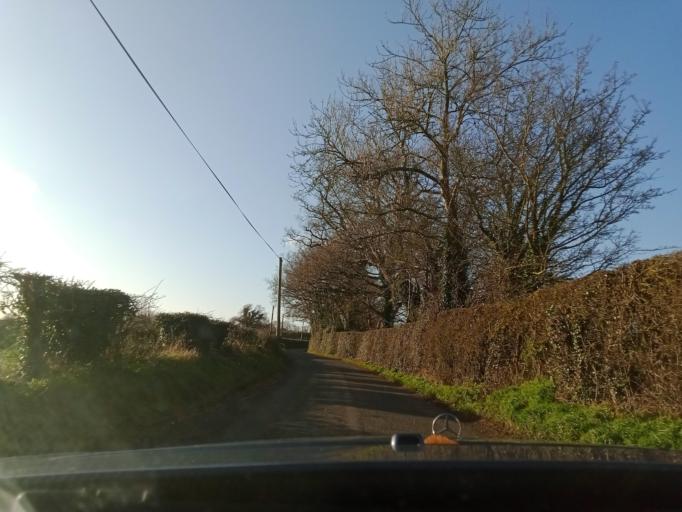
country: IE
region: Leinster
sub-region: Kilkenny
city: Callan
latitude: 52.5008
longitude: -7.3752
